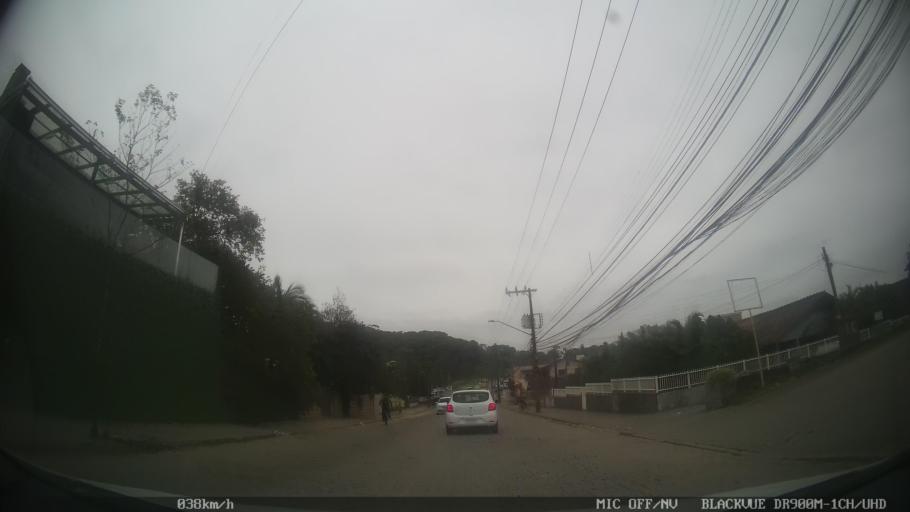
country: BR
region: Santa Catarina
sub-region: Joinville
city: Joinville
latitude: -26.3336
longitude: -48.8578
